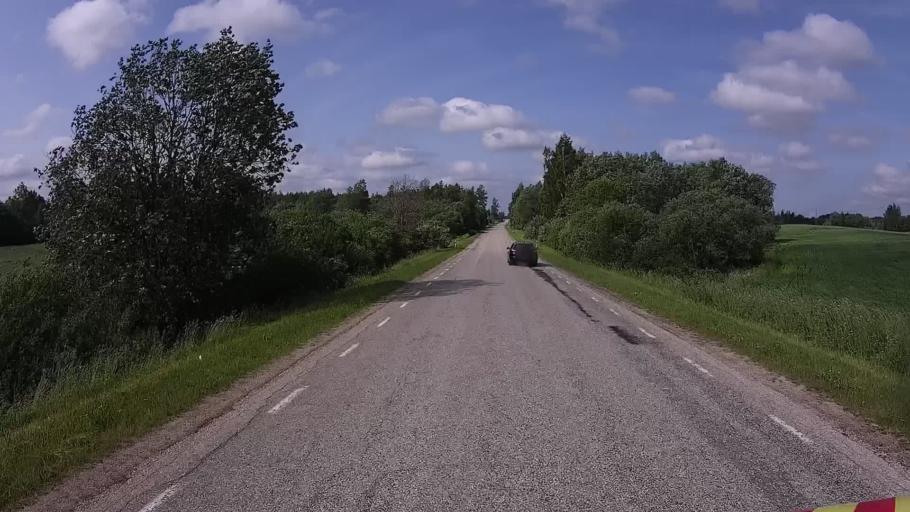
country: EE
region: Vorumaa
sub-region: Antsla vald
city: Vana-Antsla
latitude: 57.8505
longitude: 26.5807
